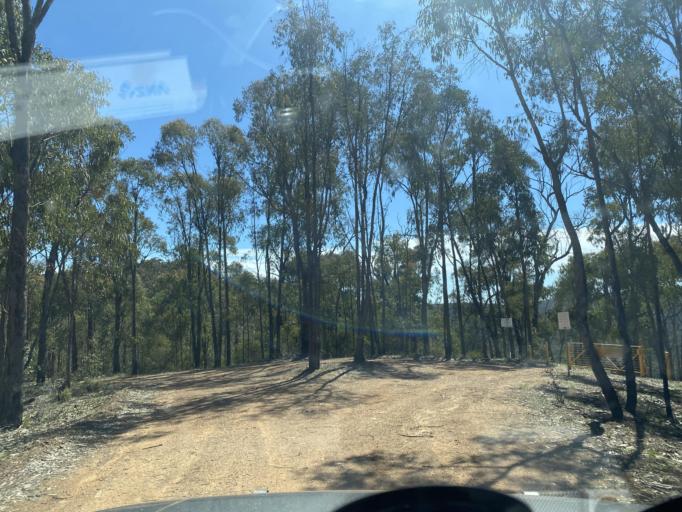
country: AU
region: Victoria
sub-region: Benalla
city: Benalla
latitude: -36.7315
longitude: 146.1830
